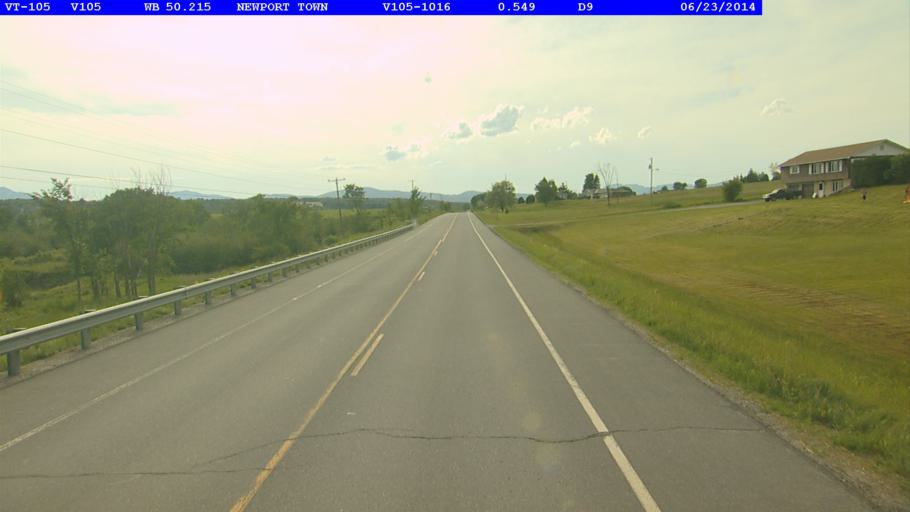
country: US
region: Vermont
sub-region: Orleans County
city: Newport
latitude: 44.9751
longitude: -72.3257
